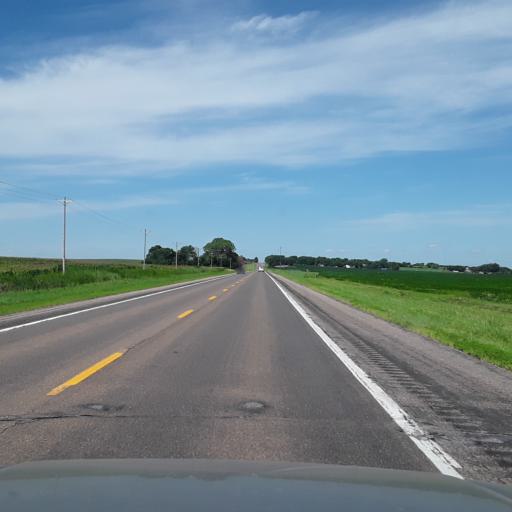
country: US
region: Nebraska
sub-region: Seward County
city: Seward
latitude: 40.9017
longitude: -97.1277
